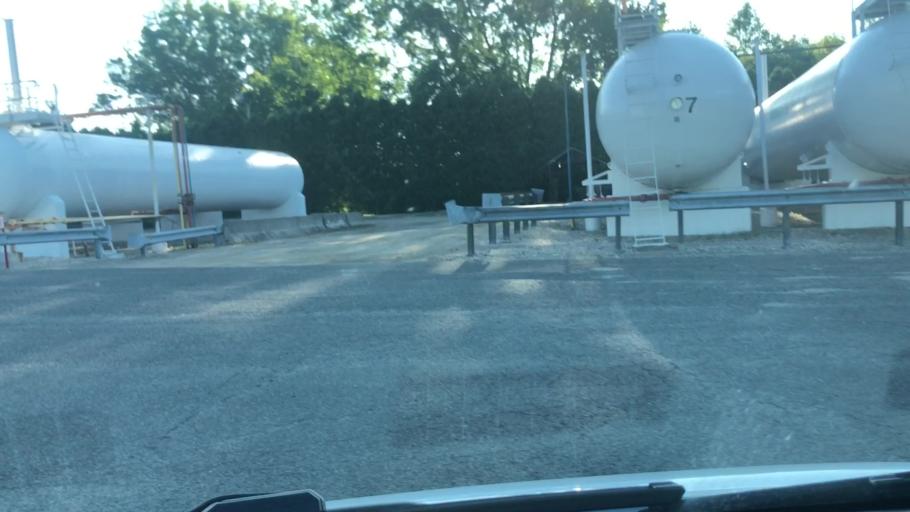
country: US
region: Massachusetts
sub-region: Berkshire County
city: Pittsfield
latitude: 42.4526
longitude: -73.2140
